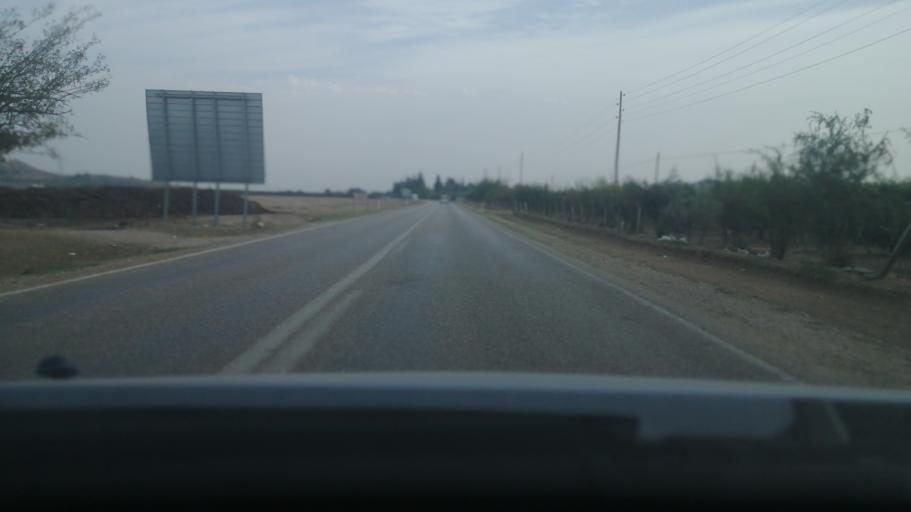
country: TR
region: Adana
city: Kozan
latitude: 37.3773
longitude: 35.8313
